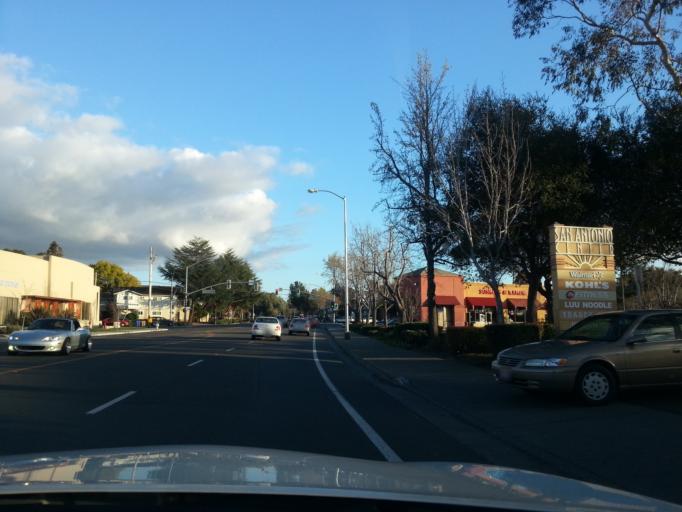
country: US
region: California
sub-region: Santa Clara County
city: Los Altos
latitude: 37.4039
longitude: -122.1069
